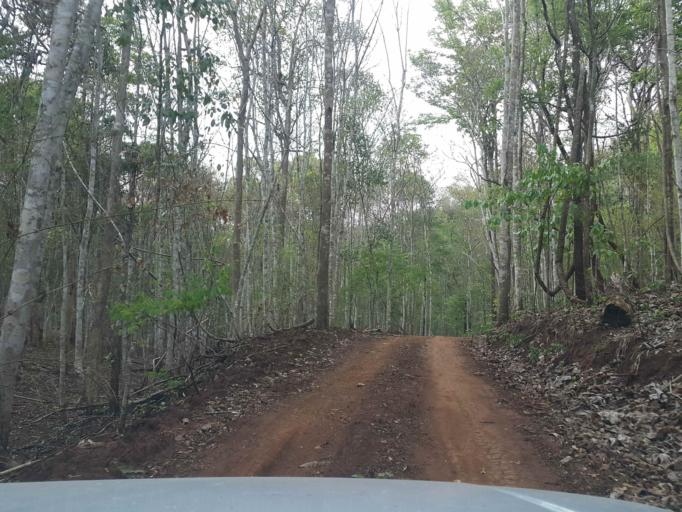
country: TH
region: Chiang Mai
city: Wiang Haeng
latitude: 19.3338
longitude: 98.7185
